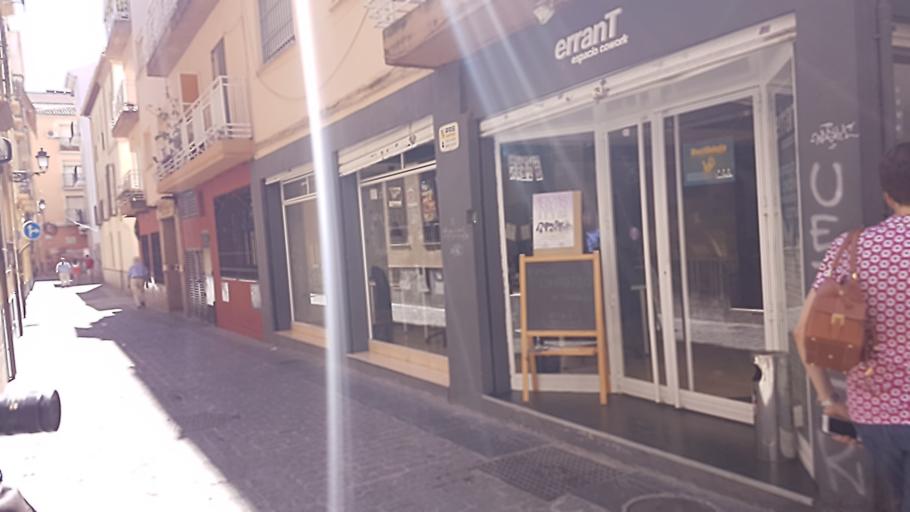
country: ES
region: Andalusia
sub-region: Provincia de Granada
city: Granada
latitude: 37.1733
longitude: -3.6028
